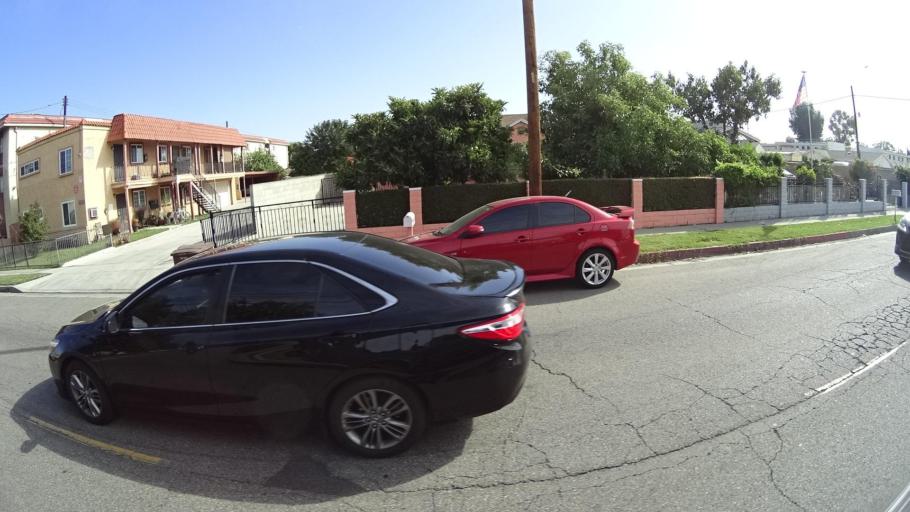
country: US
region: California
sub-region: Los Angeles County
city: West Puente Valley
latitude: 34.0362
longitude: -117.9714
